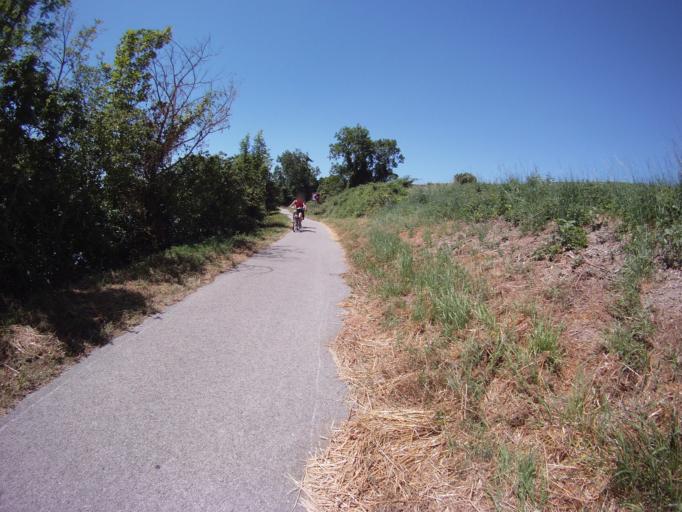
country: FR
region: Champagne-Ardenne
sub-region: Departement de la Marne
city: Mardeuil
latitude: 49.0725
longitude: 3.9406
